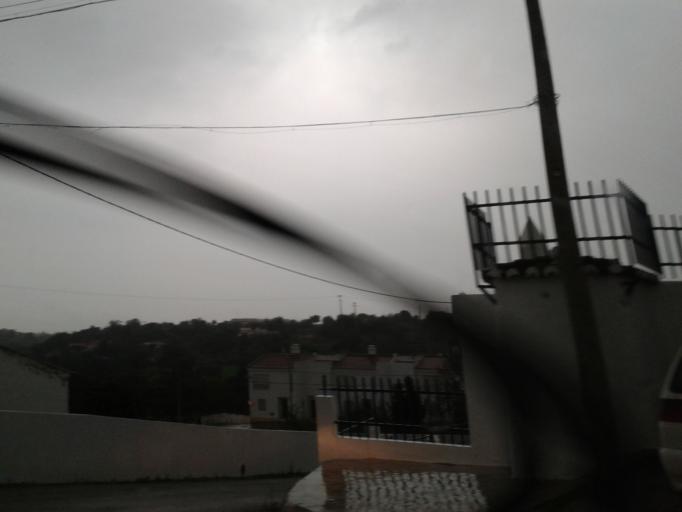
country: PT
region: Faro
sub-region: Lagoa
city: Carvoeiro
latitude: 37.1094
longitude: -8.4558
